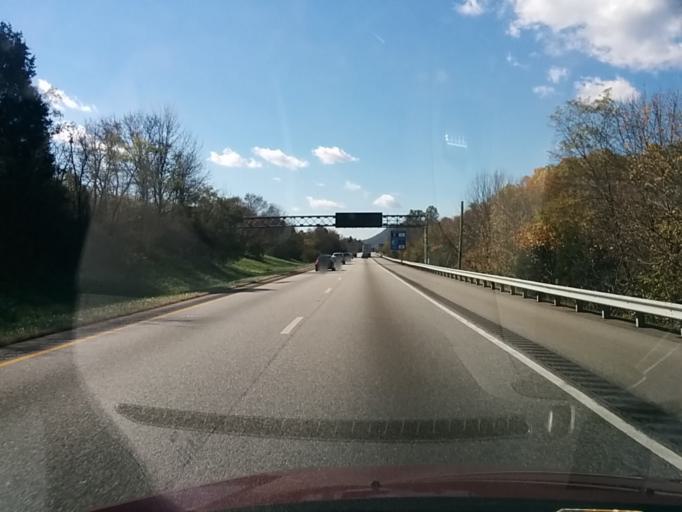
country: US
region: Virginia
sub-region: Botetourt County
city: Daleville
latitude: 37.4151
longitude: -79.8869
